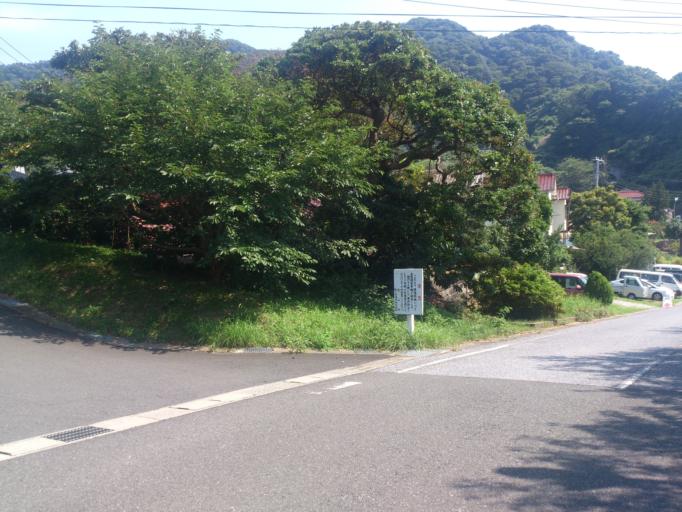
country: JP
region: Chiba
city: Tateyama
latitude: 35.0794
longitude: 139.8388
